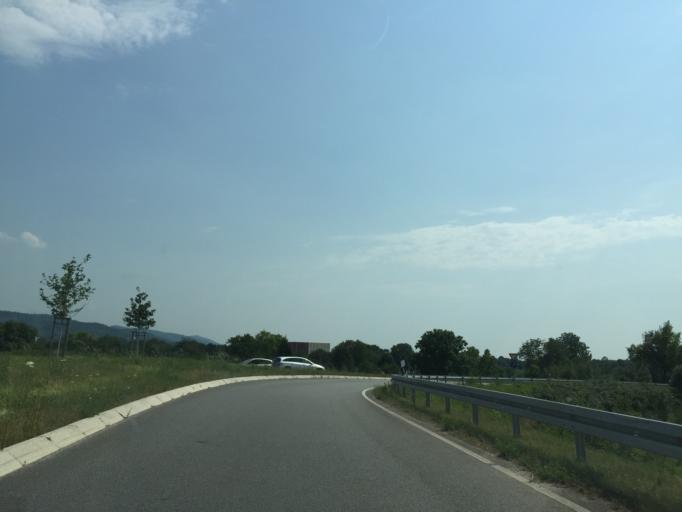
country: DE
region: Baden-Wuerttemberg
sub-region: Karlsruhe Region
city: Hemsbach
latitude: 49.5702
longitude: 8.6563
